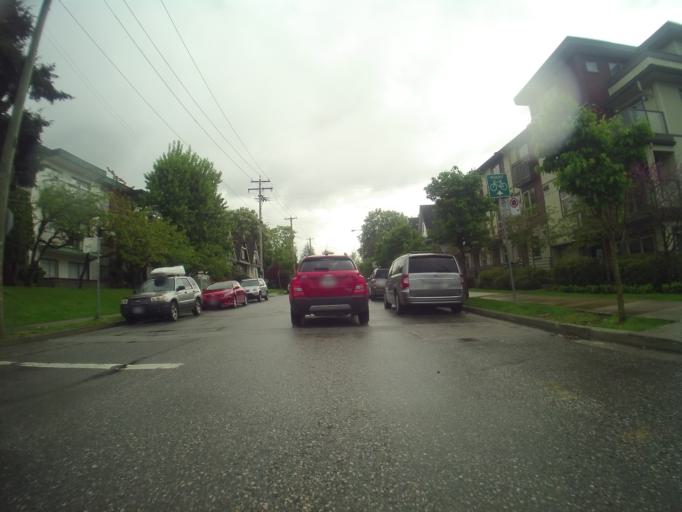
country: CA
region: British Columbia
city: Vancouver
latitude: 49.2623
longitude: -123.0737
